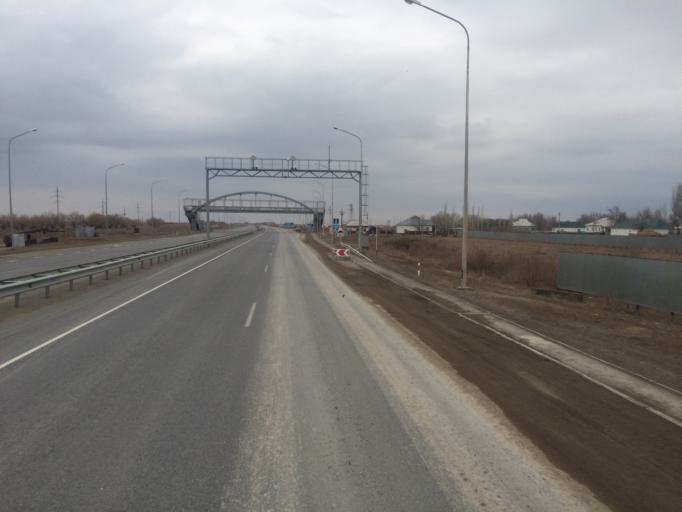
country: KZ
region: Qyzylorda
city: Shieli
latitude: 44.1370
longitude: 66.9698
